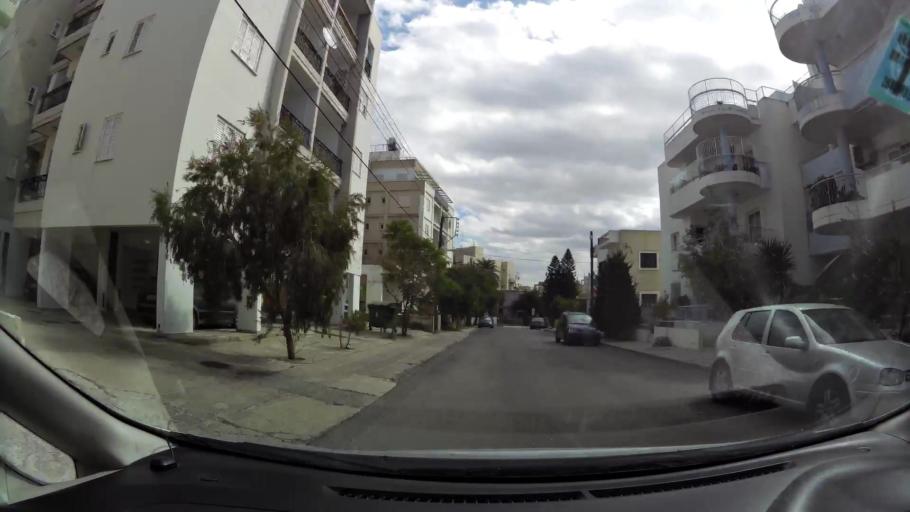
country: CY
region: Lefkosia
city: Nicosia
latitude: 35.1522
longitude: 33.3682
